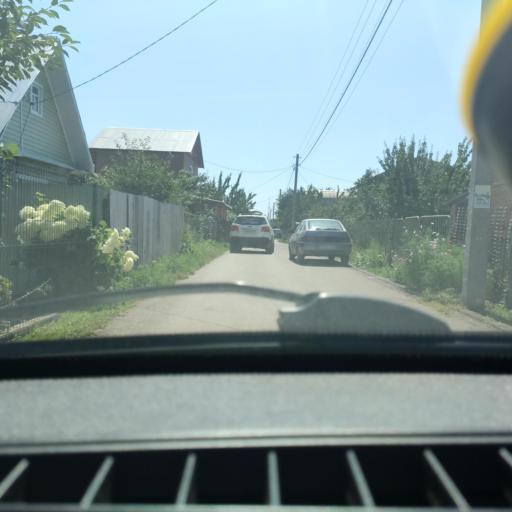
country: RU
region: Samara
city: Tol'yatti
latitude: 53.5950
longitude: 49.3055
